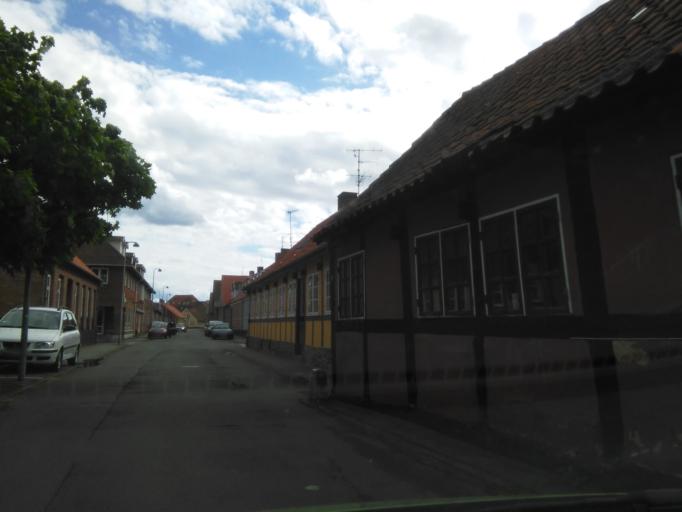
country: DK
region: Capital Region
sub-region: Bornholm Kommune
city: Nexo
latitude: 55.0654
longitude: 15.1328
